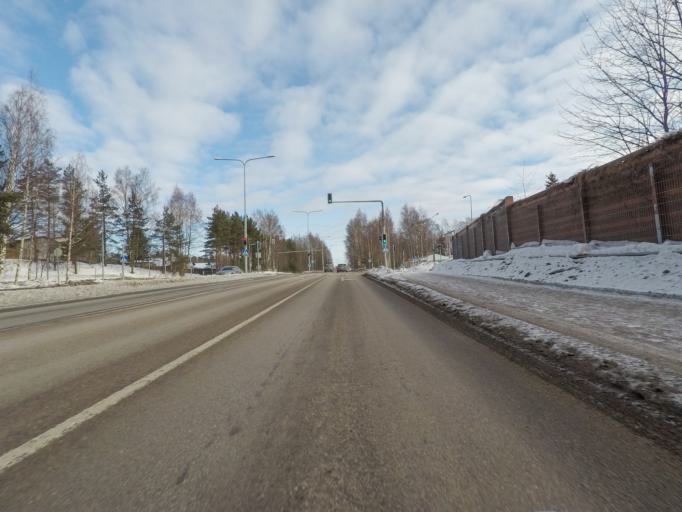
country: FI
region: Uusimaa
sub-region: Helsinki
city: Vantaa
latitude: 60.2209
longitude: 25.1095
